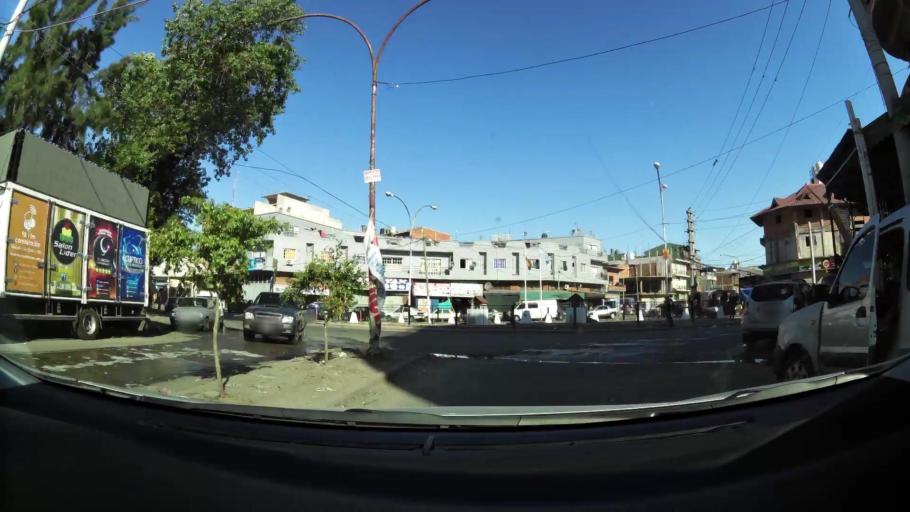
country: AR
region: Buenos Aires F.D.
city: Villa Lugano
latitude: -34.7004
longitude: -58.4827
